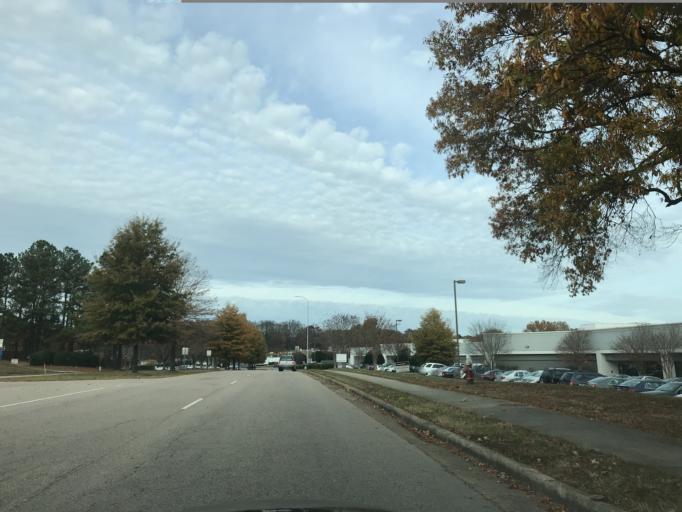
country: US
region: North Carolina
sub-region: Wake County
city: Raleigh
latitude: 35.8526
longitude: -78.5862
